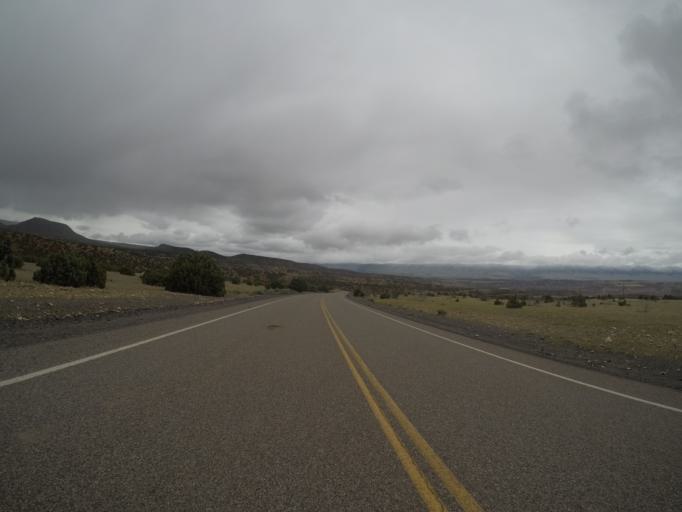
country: US
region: Wyoming
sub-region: Big Horn County
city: Lovell
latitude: 45.0985
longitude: -108.2477
